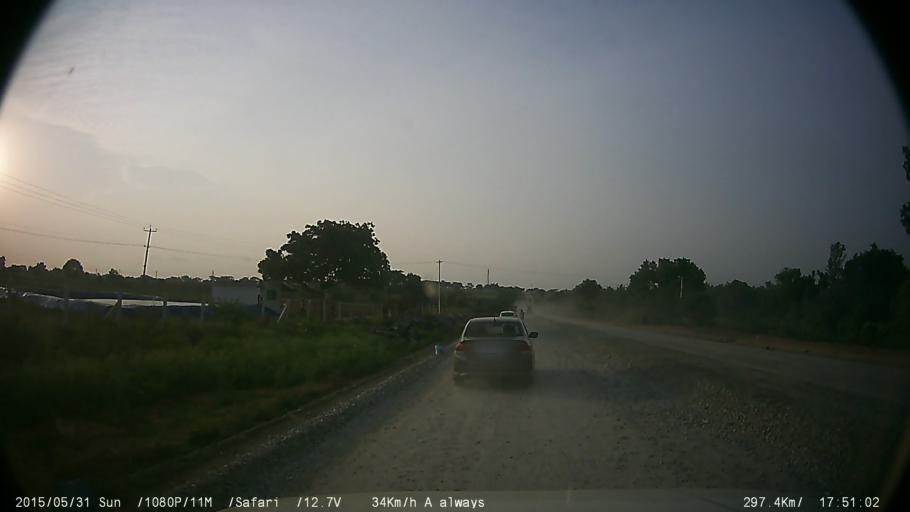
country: IN
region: Karnataka
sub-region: Mysore
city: Nanjangud
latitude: 11.9758
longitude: 76.6697
